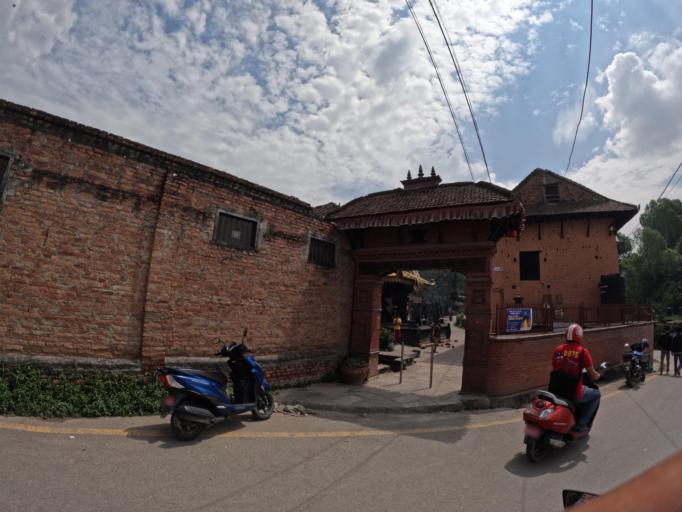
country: NP
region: Central Region
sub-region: Bagmati Zone
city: Bhaktapur
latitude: 27.6806
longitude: 85.3829
